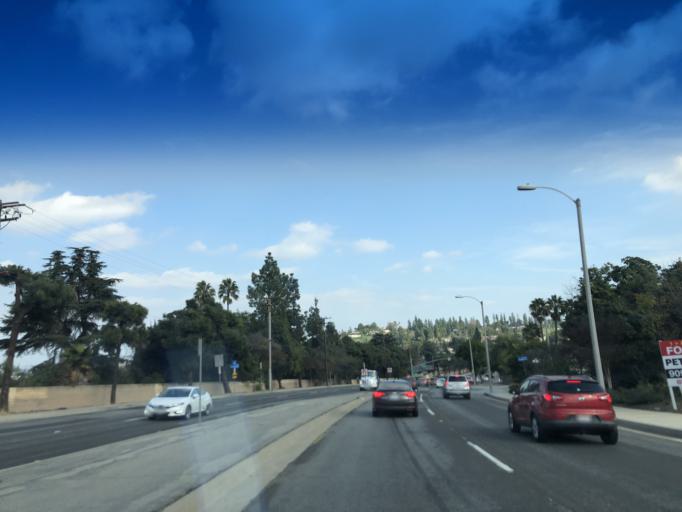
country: US
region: California
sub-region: Los Angeles County
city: Hacienda Heights
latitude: 33.9801
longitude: -117.9793
